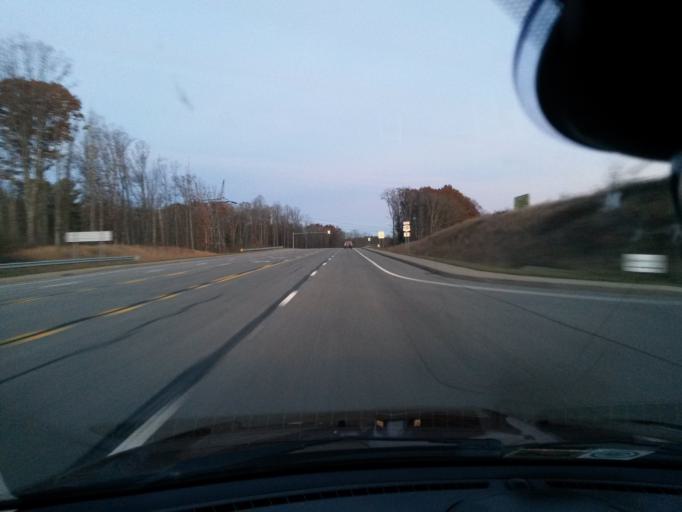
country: US
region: West Virginia
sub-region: Raleigh County
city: Stanaford
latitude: 37.7879
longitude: -81.1585
